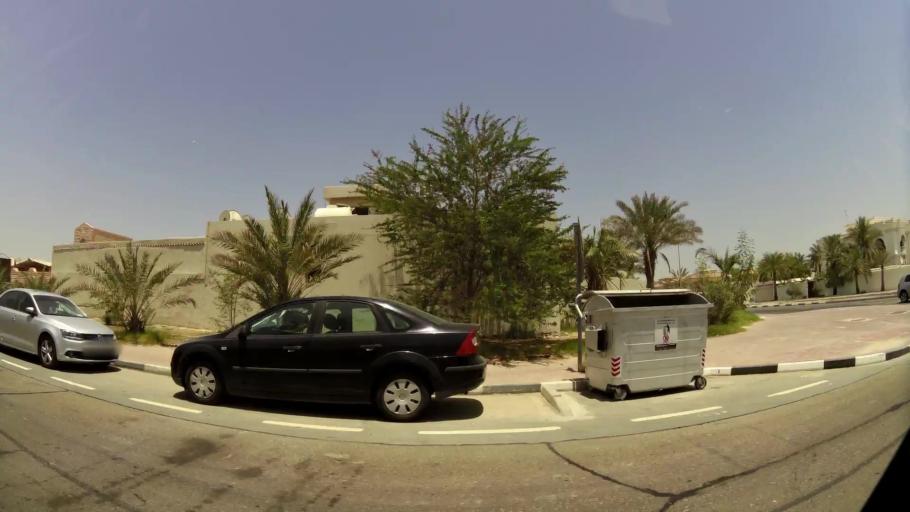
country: AE
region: Dubai
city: Dubai
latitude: 25.1955
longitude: 55.2519
